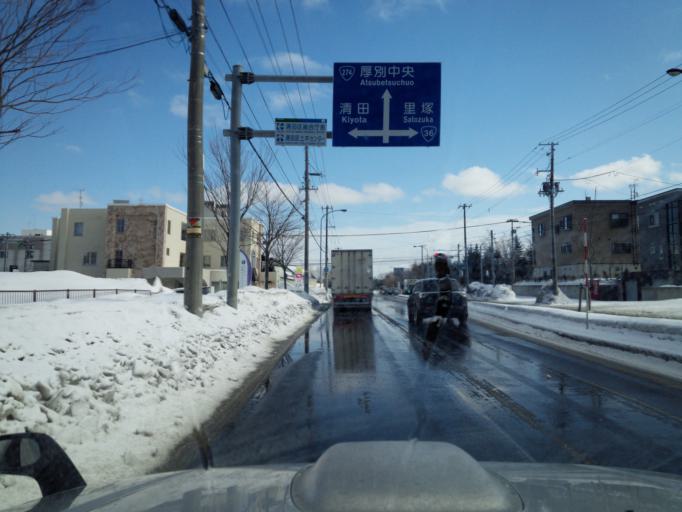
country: JP
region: Hokkaido
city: Kitahiroshima
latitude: 42.9911
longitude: 141.4527
